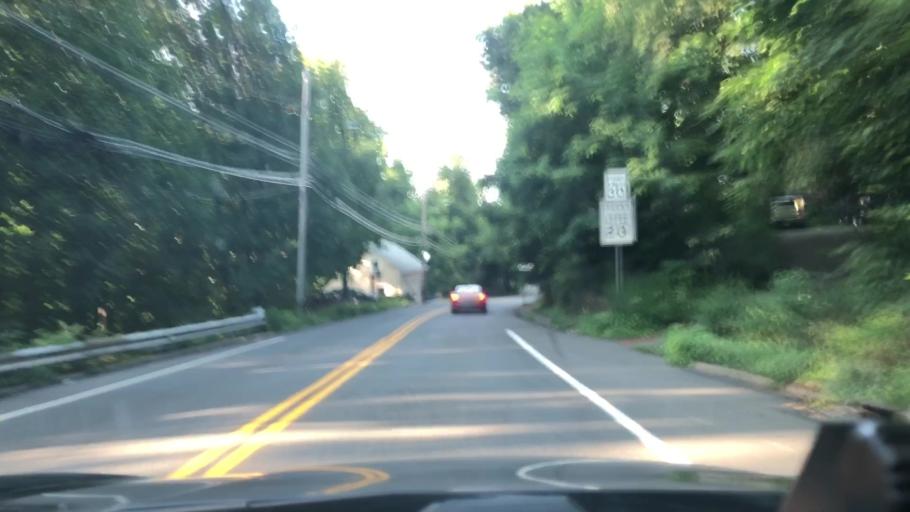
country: US
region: Pennsylvania
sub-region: Lehigh County
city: Fountain Hill
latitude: 40.6005
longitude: -75.3887
